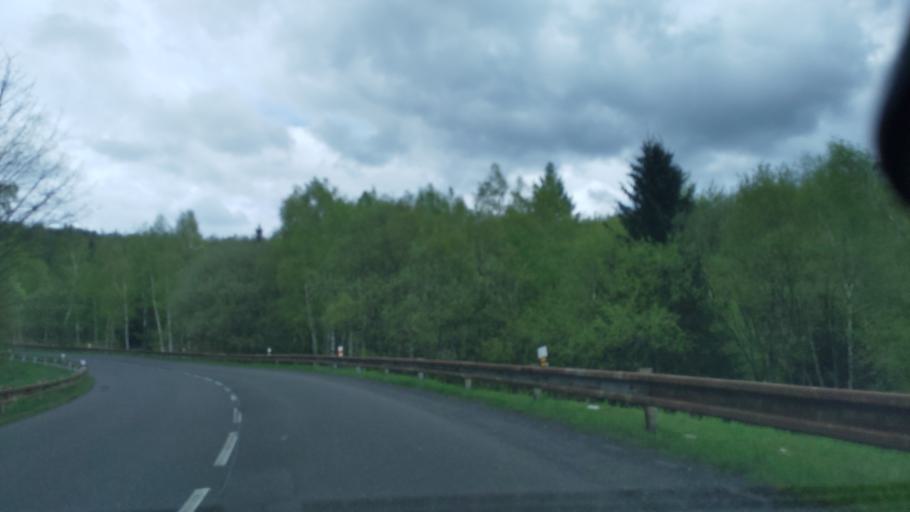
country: CZ
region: Ustecky
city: Libouchec
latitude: 50.7834
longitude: 14.0411
